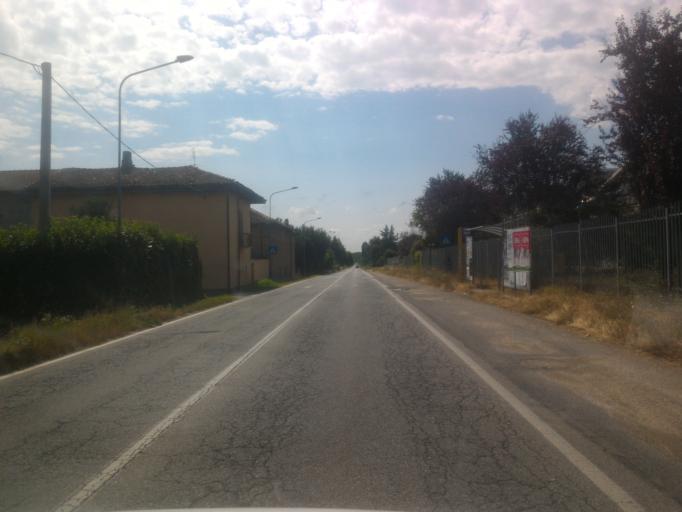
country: IT
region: Piedmont
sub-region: Provincia di Torino
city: Cumiana
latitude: 44.9659
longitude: 7.3955
